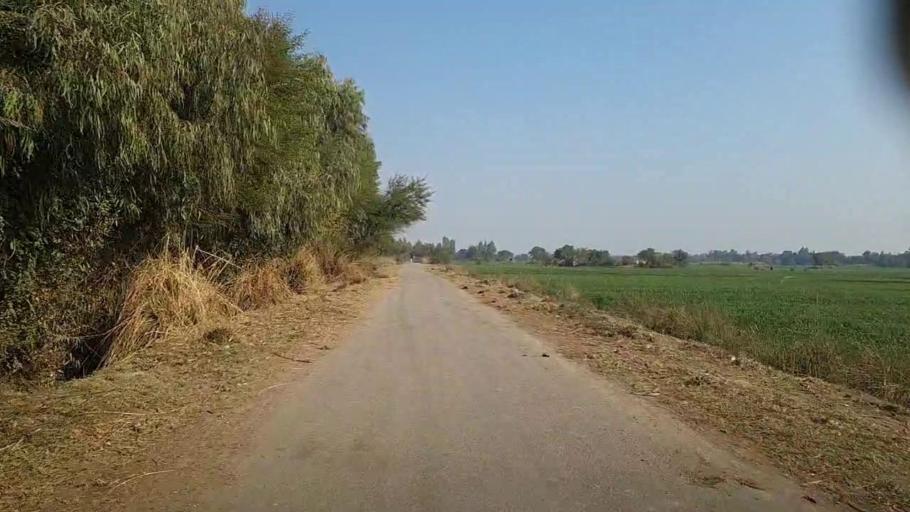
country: PK
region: Sindh
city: Mirpur Mathelo
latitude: 27.8771
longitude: 69.6121
